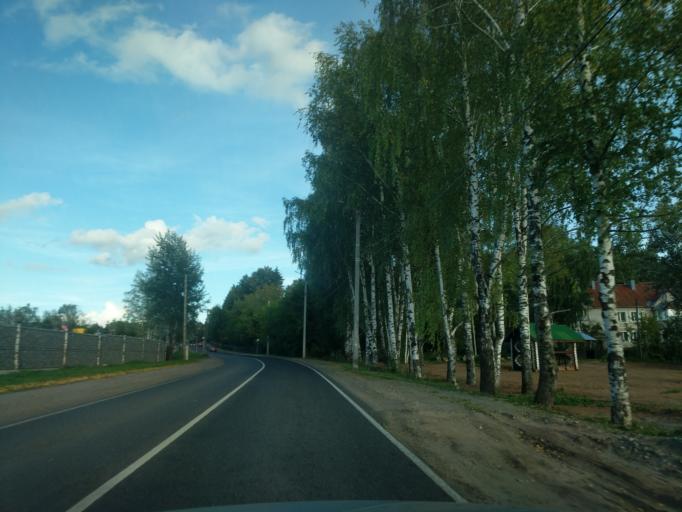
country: RU
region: Kirov
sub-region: Kirovo-Chepetskiy Rayon
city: Kirov
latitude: 58.6115
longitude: 49.7847
